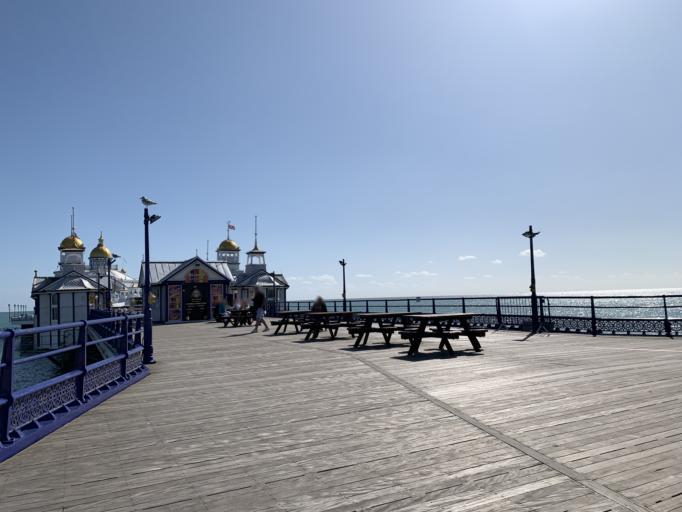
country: GB
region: England
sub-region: East Sussex
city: Eastbourne
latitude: 50.7669
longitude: 0.2936
